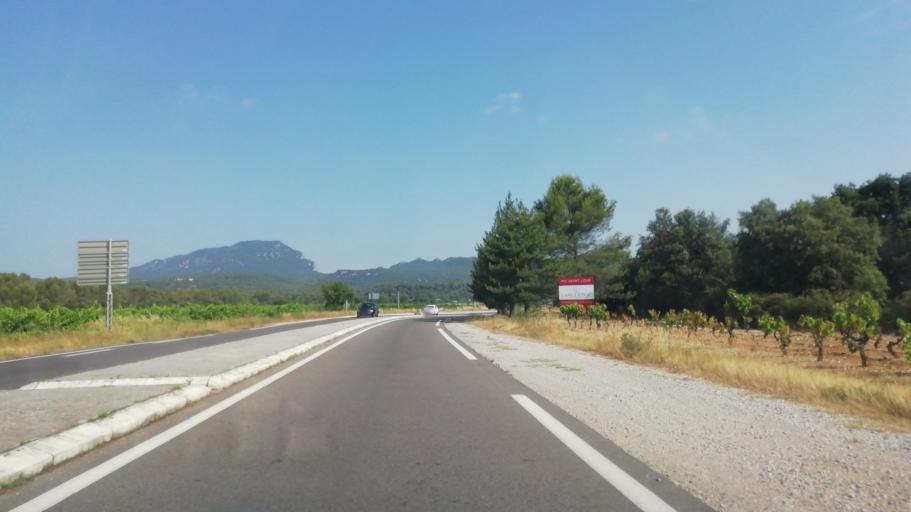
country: FR
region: Languedoc-Roussillon
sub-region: Departement de l'Herault
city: Saint-Mathieu-de-Treviers
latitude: 43.7471
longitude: 3.8595
